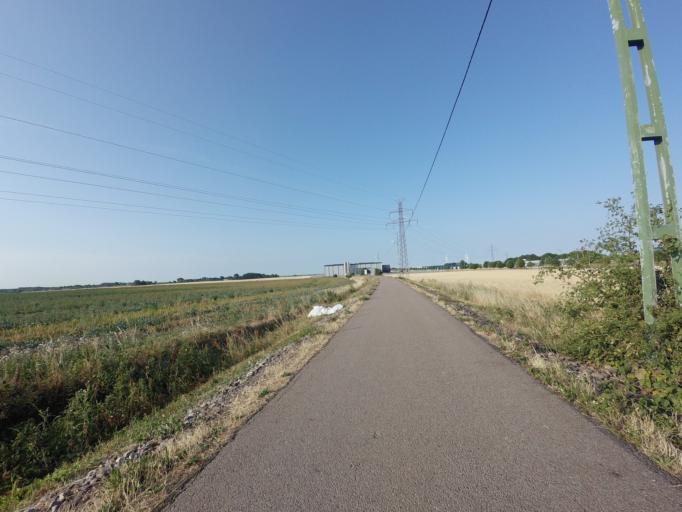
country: SE
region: Skane
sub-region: Landskrona
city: Asmundtorp
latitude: 55.8747
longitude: 12.8904
